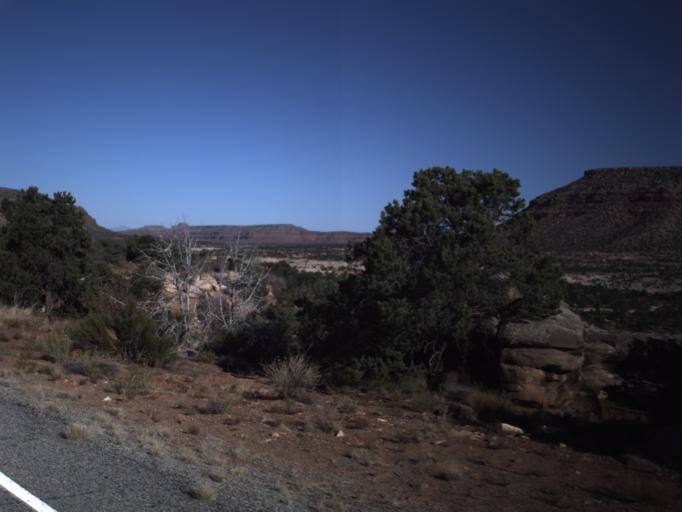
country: US
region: Utah
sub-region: San Juan County
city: Blanding
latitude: 37.5978
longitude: -110.0507
